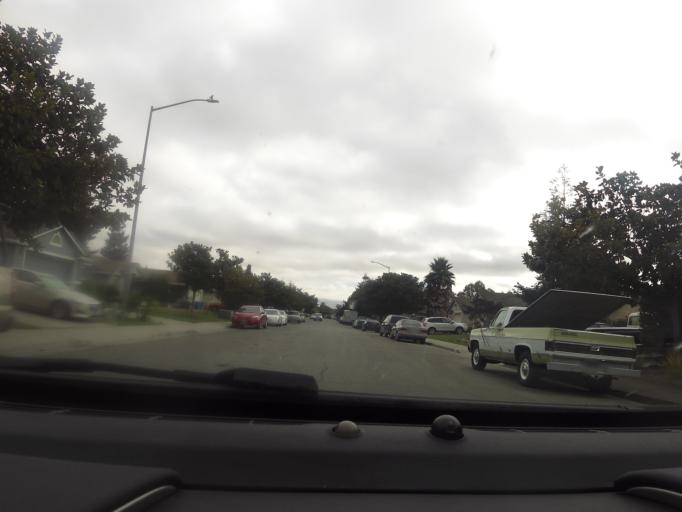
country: US
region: California
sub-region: San Benito County
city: Hollister
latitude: 36.8472
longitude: -121.3895
